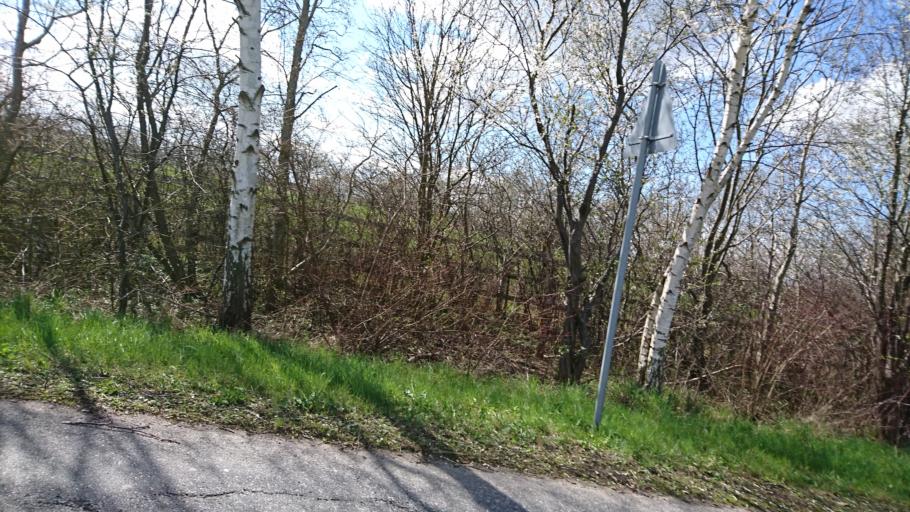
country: DK
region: Capital Region
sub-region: Egedal Kommune
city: Ganlose
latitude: 55.7977
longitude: 12.2569
